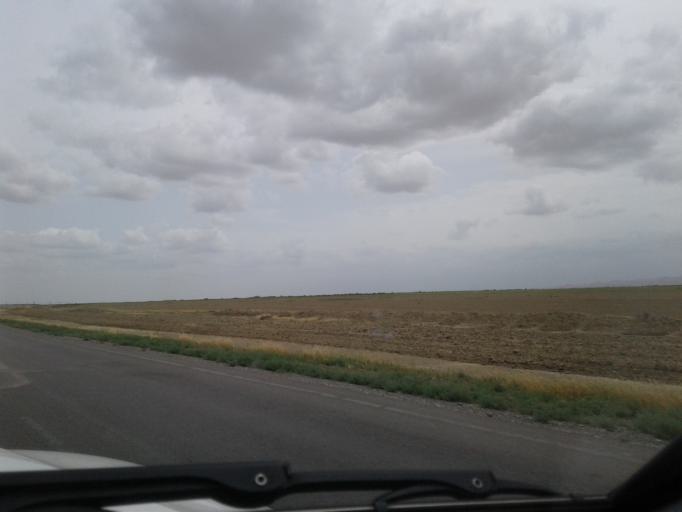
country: IR
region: Razavi Khorasan
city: Dargaz
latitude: 37.5930
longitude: 59.2791
